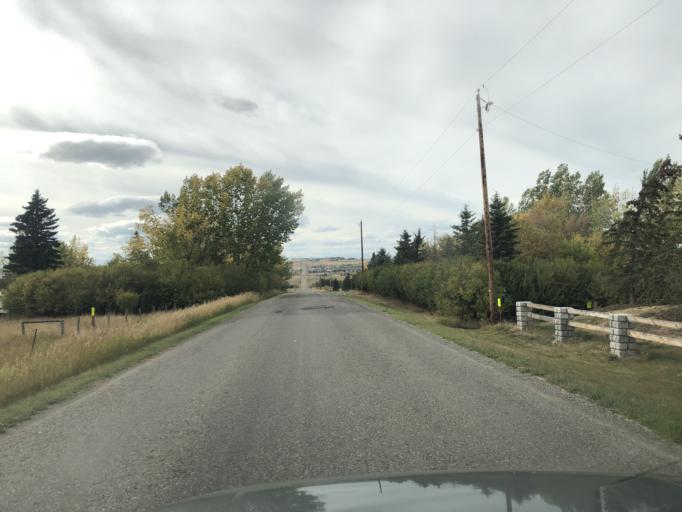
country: CA
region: Alberta
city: Okotoks
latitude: 50.6886
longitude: -113.9683
